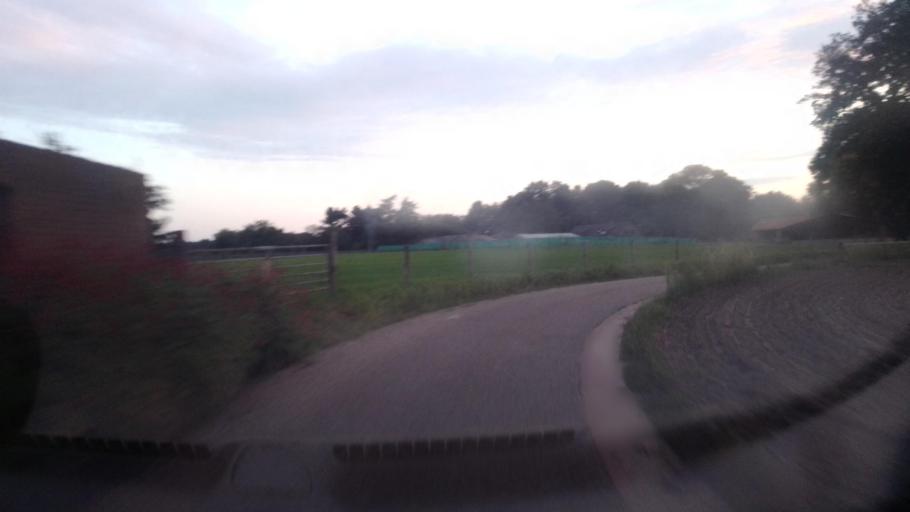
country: NL
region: Limburg
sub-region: Gemeente Peel en Maas
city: Maasbree
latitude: 51.3526
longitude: 6.0313
